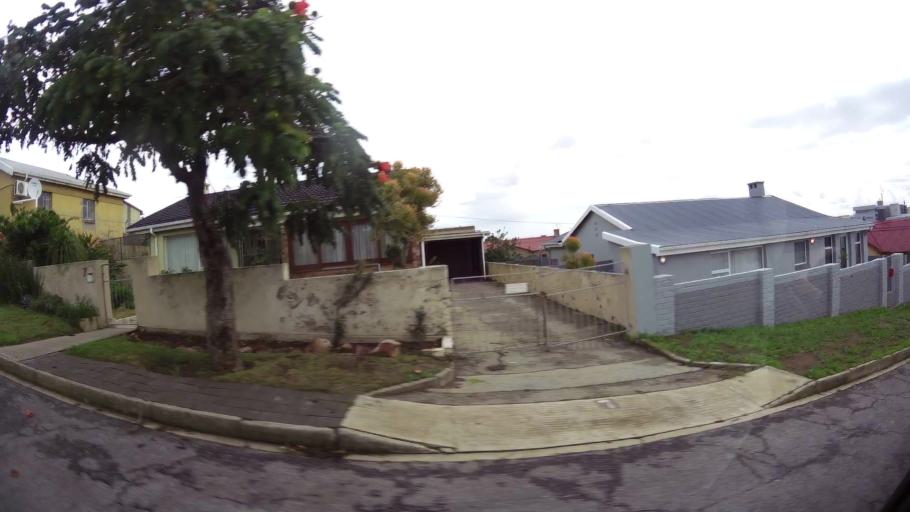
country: ZA
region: Eastern Cape
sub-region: Nelson Mandela Bay Metropolitan Municipality
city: Port Elizabeth
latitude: -33.9393
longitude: 25.5867
